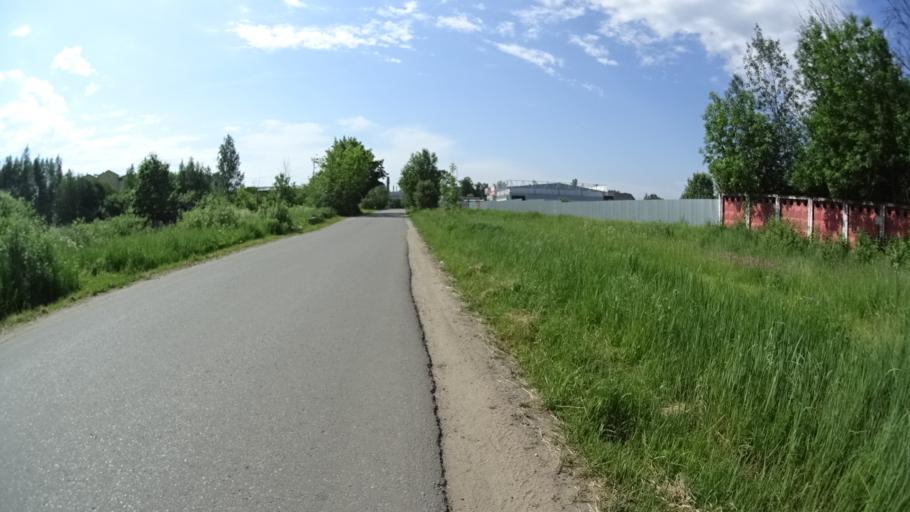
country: RU
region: Moskovskaya
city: Zelenogradskiy
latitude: 56.0882
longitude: 37.9322
